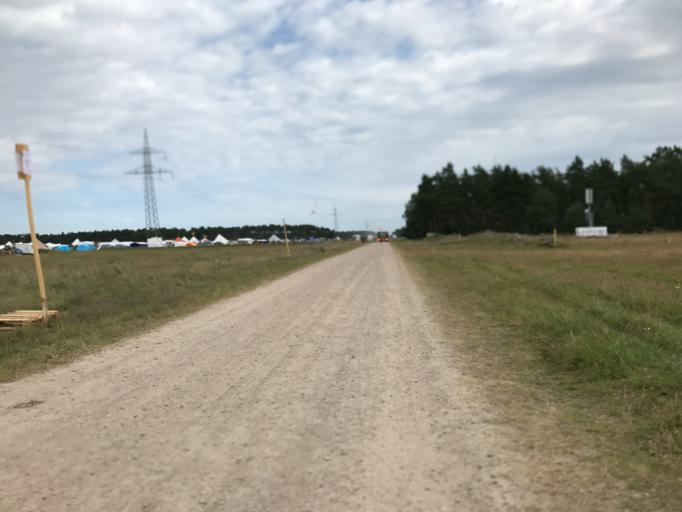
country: SE
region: Skane
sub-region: Kristianstads Kommun
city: Fjalkinge
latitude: 56.0011
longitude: 14.2983
